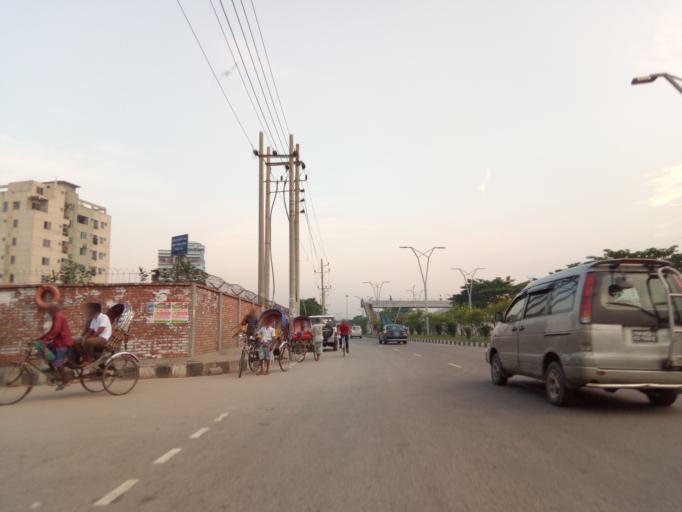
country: BD
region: Dhaka
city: Paltan
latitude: 23.7653
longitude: 90.4124
